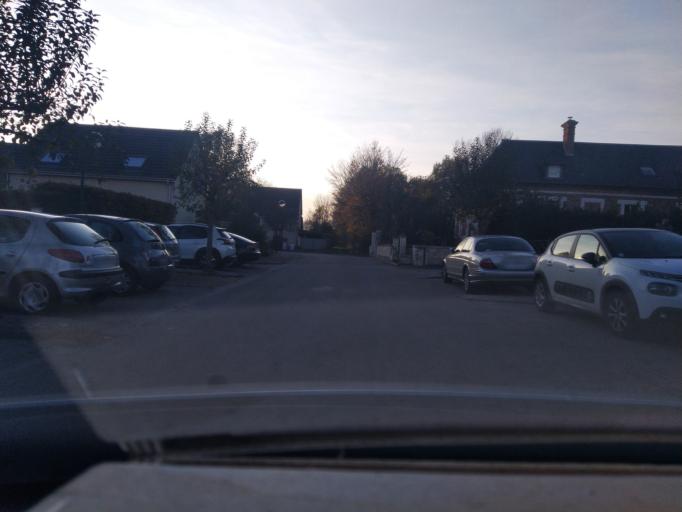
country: FR
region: Haute-Normandie
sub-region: Departement de la Seine-Maritime
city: Yainville
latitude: 49.4540
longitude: 0.8296
